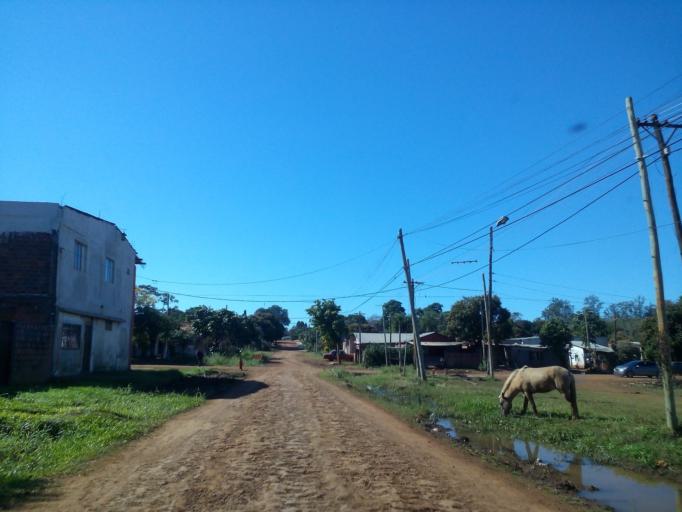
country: AR
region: Misiones
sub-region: Departamento de Capital
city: Posadas
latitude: -27.3910
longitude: -55.9243
